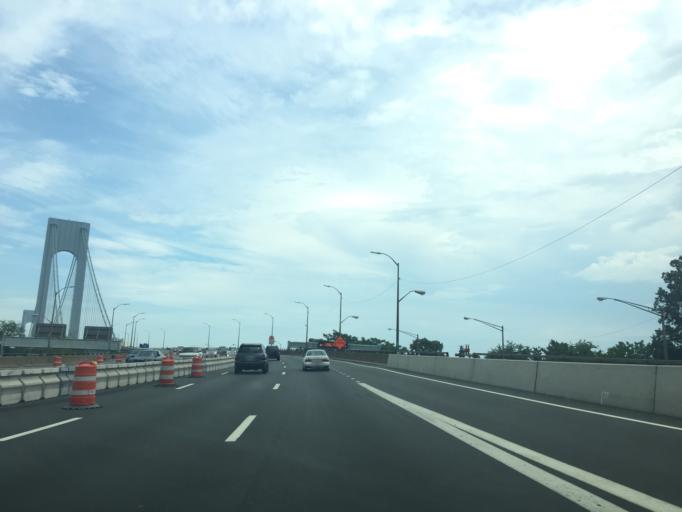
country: US
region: New York
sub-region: Kings County
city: Bensonhurst
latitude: 40.6017
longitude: -74.0610
